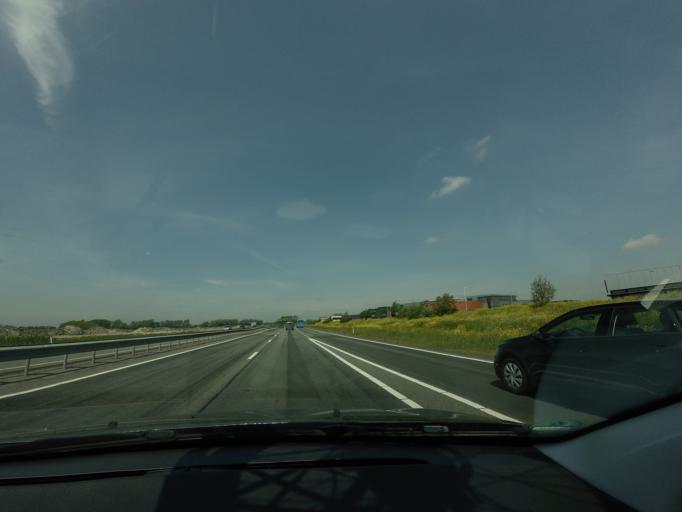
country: NL
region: Friesland
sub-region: Sudwest Fryslan
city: IJlst
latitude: 53.0352
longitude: 5.6209
